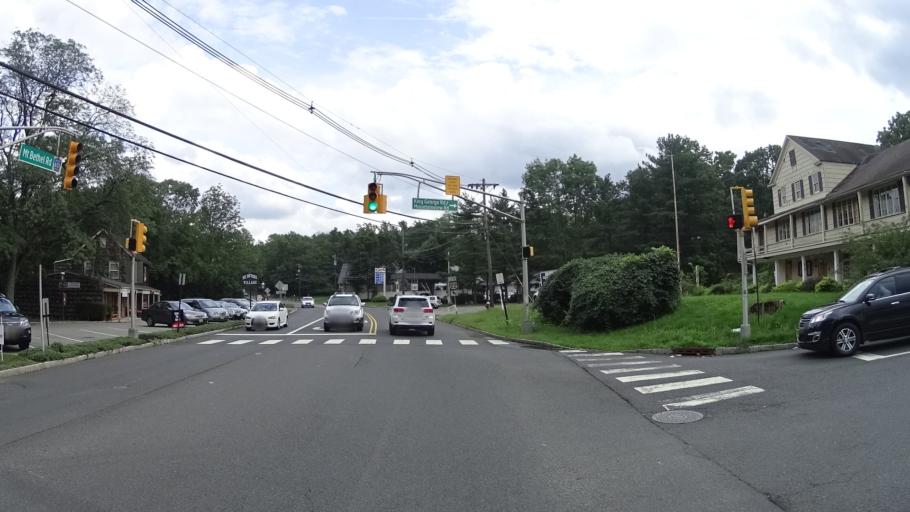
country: US
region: New Jersey
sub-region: Somerset County
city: Warren Township
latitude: 40.6379
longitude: -74.5141
